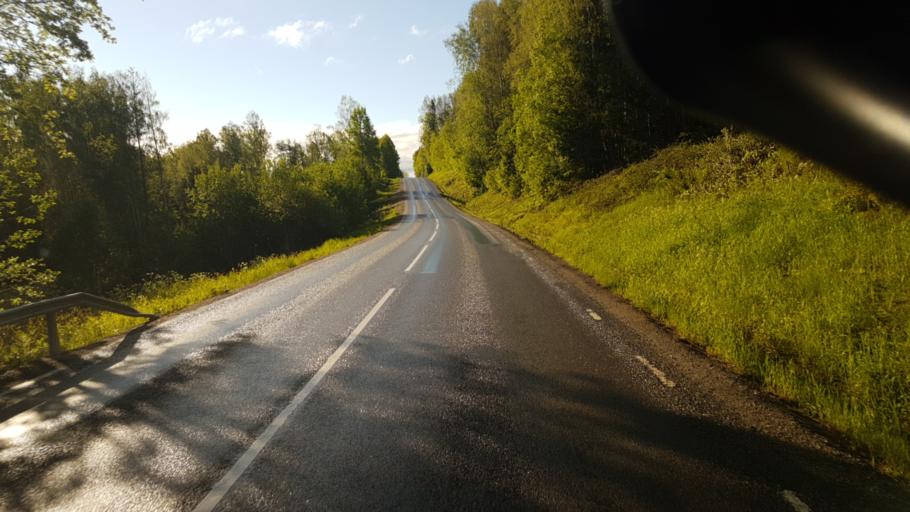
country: SE
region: Vaermland
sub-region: Eda Kommun
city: Amotfors
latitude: 59.6577
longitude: 12.4368
